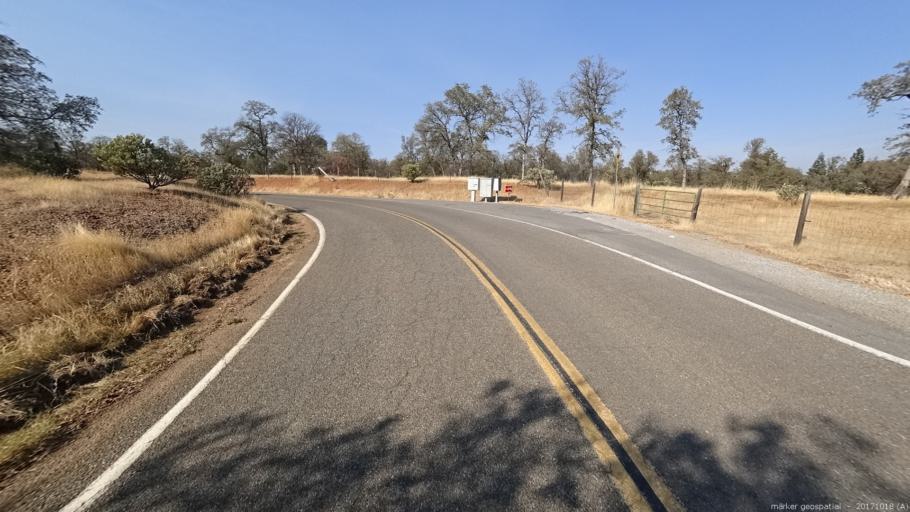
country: US
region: California
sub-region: Shasta County
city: Palo Cedro
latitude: 40.5601
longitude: -122.2574
